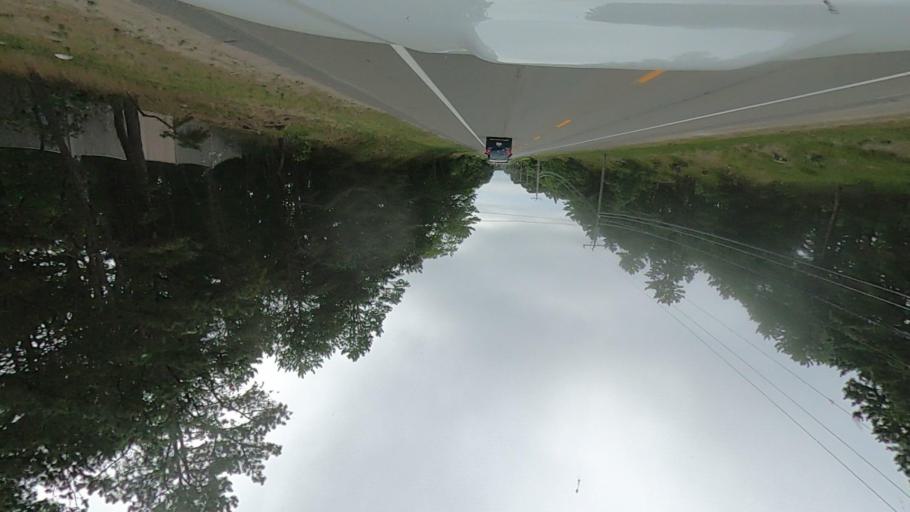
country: US
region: Massachusetts
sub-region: Barnstable County
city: North Eastham
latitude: 41.8977
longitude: -69.9856
